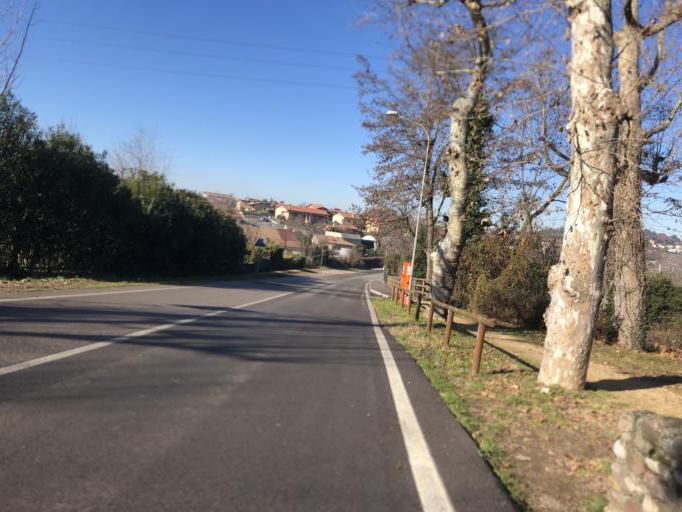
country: IT
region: Veneto
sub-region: Provincia di Verona
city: Sona
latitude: 45.4394
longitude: 10.8249
